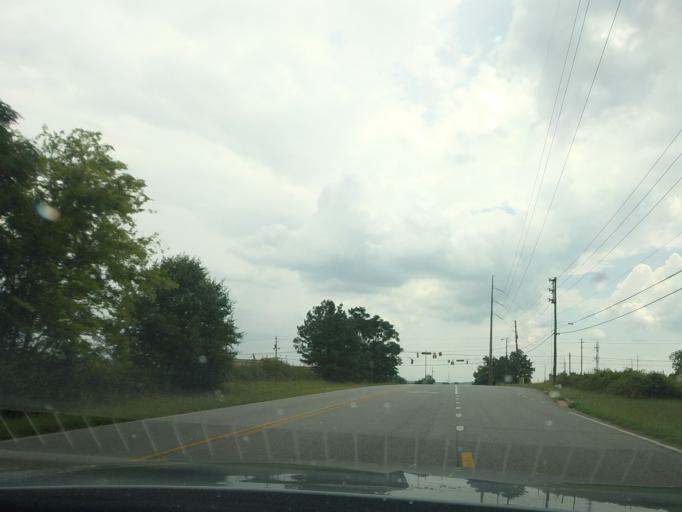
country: US
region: Georgia
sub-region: Bibb County
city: West Point
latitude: 32.8107
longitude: -83.7456
